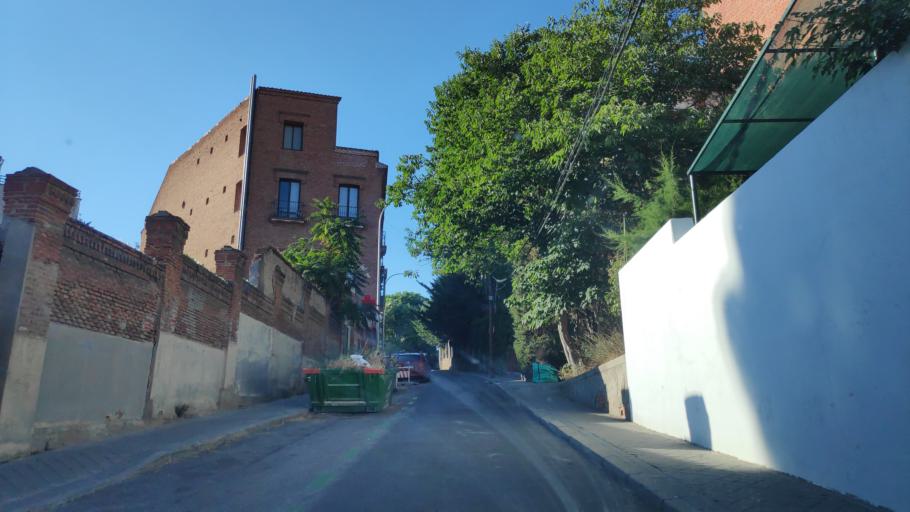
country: ES
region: Madrid
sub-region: Provincia de Madrid
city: Tetuan de las Victorias
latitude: 40.4567
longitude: -3.7158
